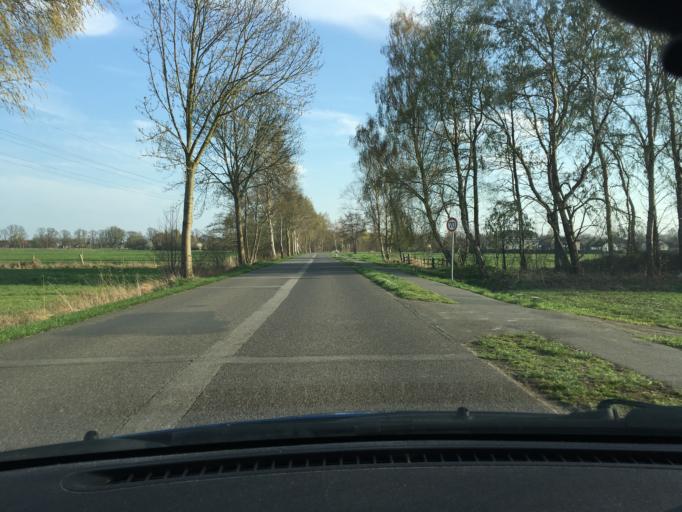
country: DE
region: Lower Saxony
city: Stelle
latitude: 53.4185
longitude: 10.0587
